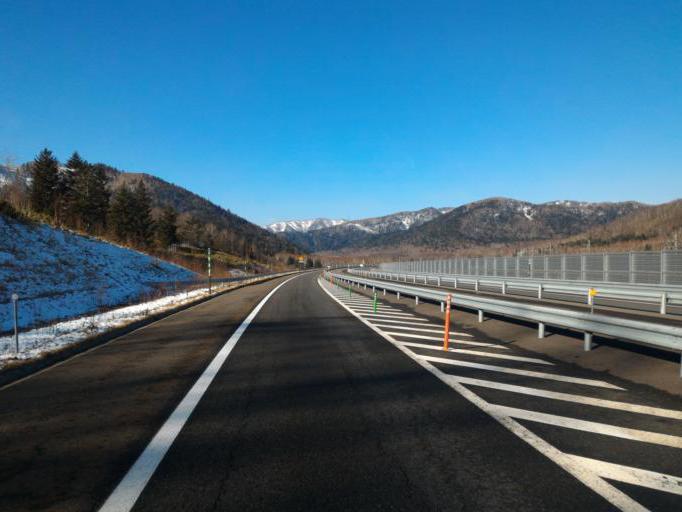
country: JP
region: Hokkaido
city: Shimo-furano
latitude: 43.0553
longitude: 142.5682
